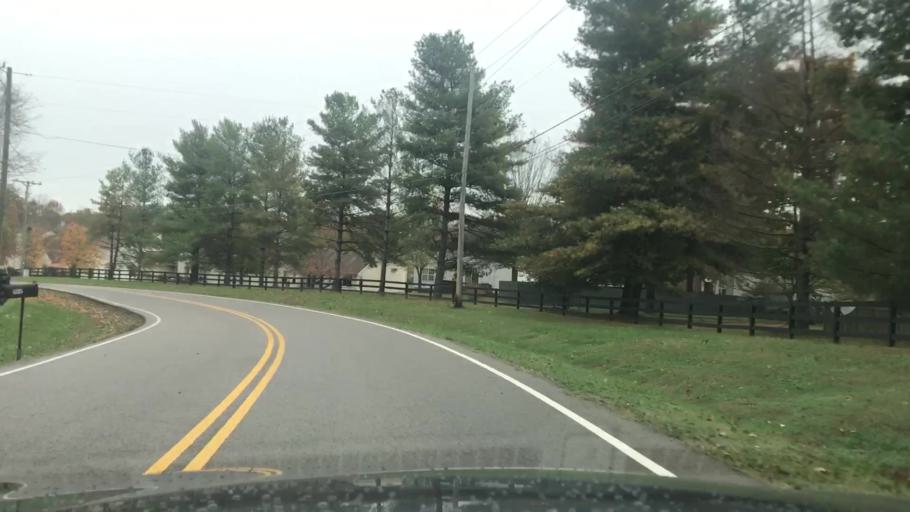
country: US
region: Tennessee
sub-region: Williamson County
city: Franklin
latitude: 35.8970
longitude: -86.8206
